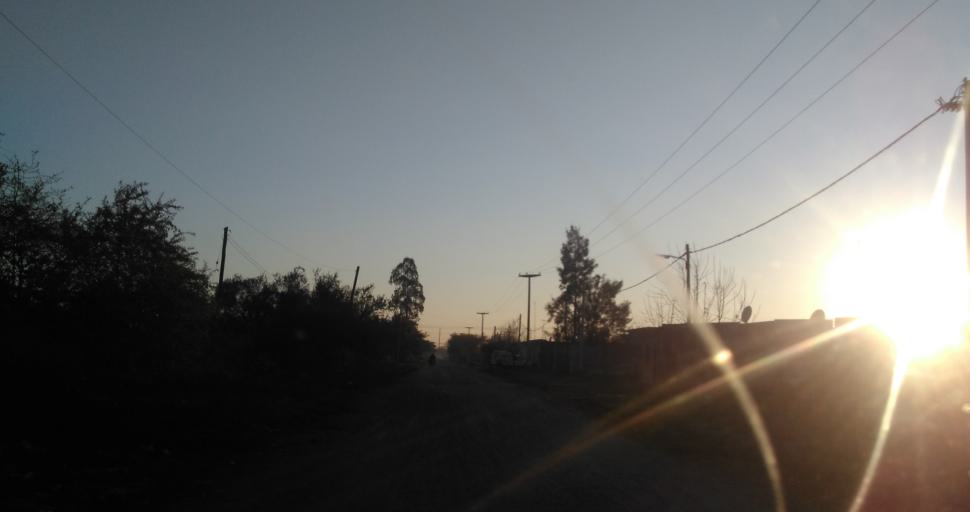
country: AR
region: Chaco
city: Resistencia
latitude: -27.4816
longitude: -59.0045
